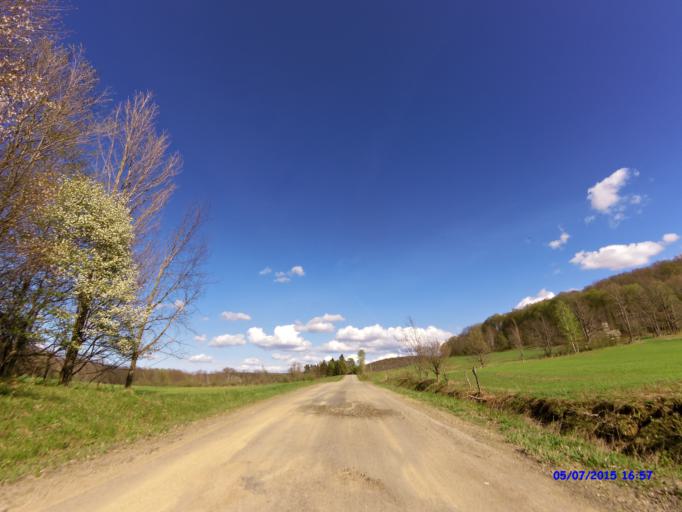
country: US
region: New York
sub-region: Cattaraugus County
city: Little Valley
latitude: 42.3018
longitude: -78.7552
